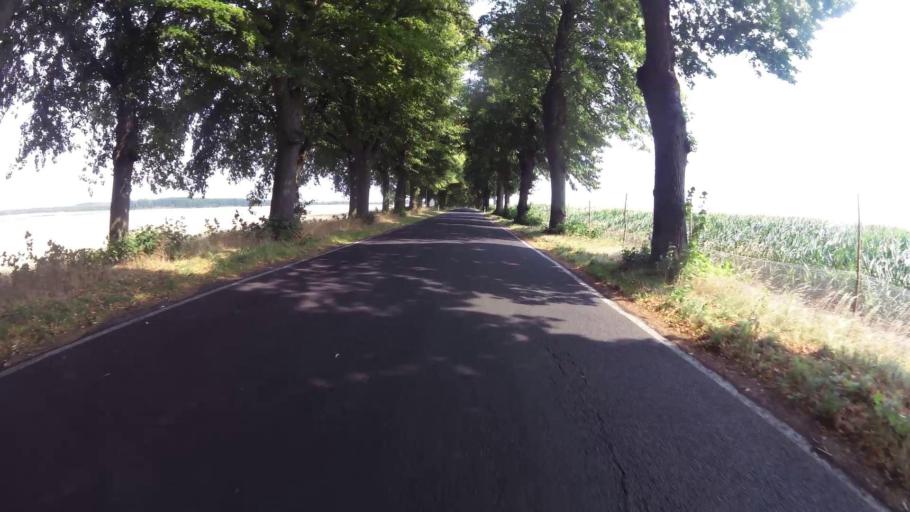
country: PL
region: West Pomeranian Voivodeship
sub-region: Powiat gryfinski
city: Mieszkowice
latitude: 52.8235
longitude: 14.4684
